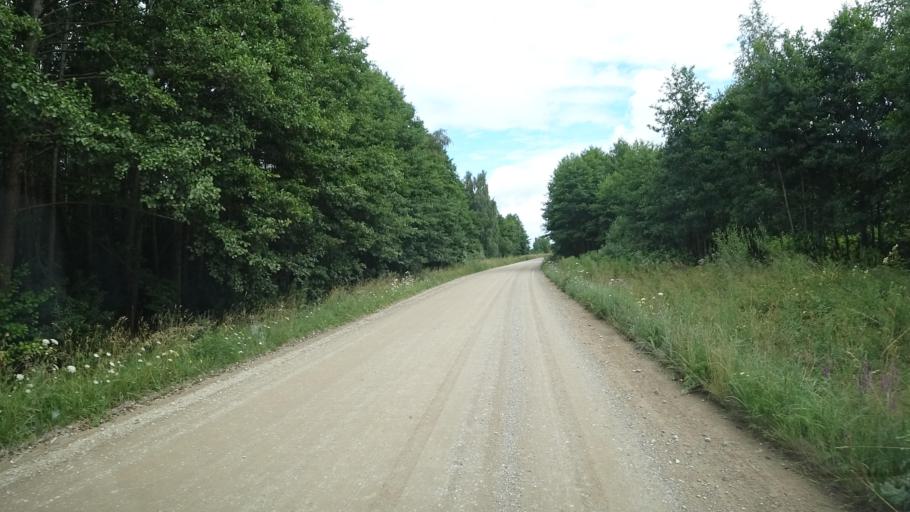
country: LV
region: Liepaja
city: Vec-Liepaja
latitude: 56.6246
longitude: 21.0446
